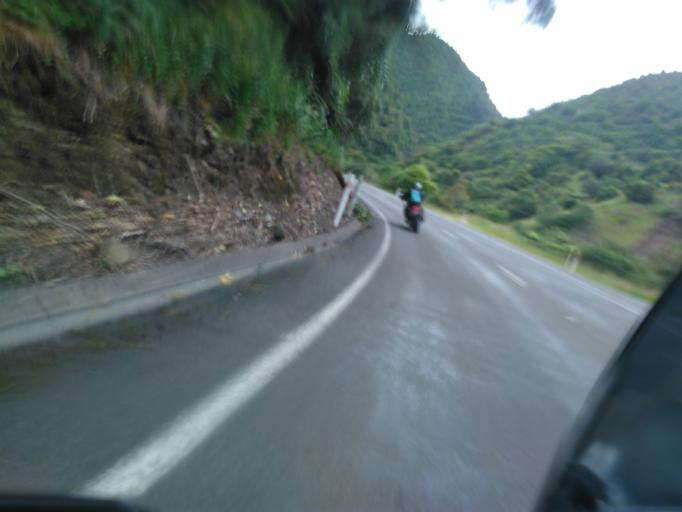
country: NZ
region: Bay of Plenty
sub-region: Opotiki District
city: Opotiki
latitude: -38.3097
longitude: 177.3930
